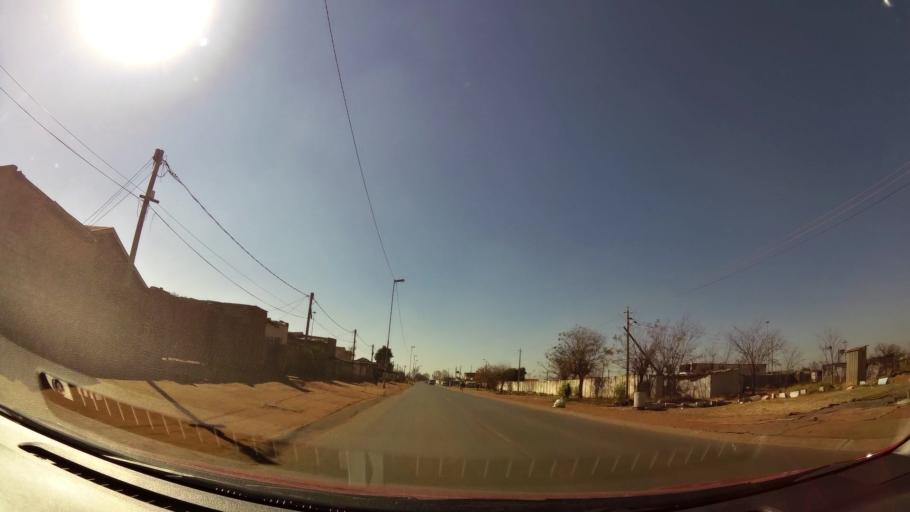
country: ZA
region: Gauteng
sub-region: City of Johannesburg Metropolitan Municipality
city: Soweto
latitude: -26.2239
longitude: 27.8305
